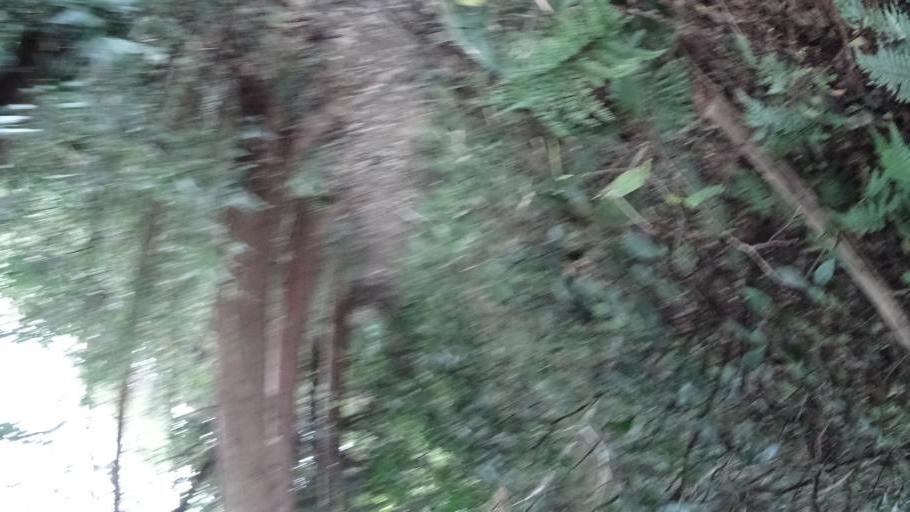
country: JP
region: Kanagawa
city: Zushi
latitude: 35.2857
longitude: 139.6168
